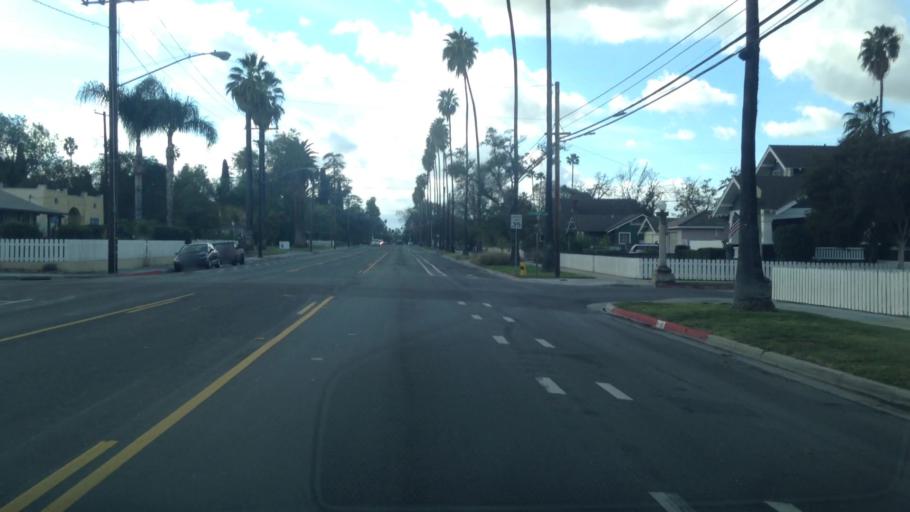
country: US
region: California
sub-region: Riverside County
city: Riverside
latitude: 33.9718
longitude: -117.3896
